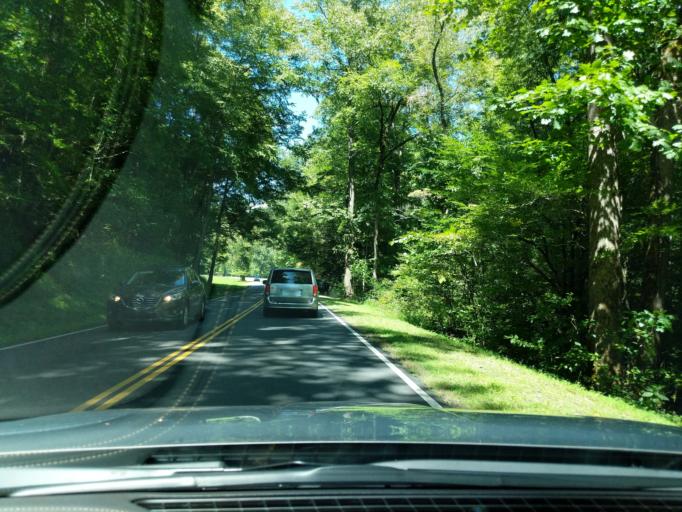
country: US
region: North Carolina
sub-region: Swain County
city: Cherokee
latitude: 35.5281
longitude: -83.3037
